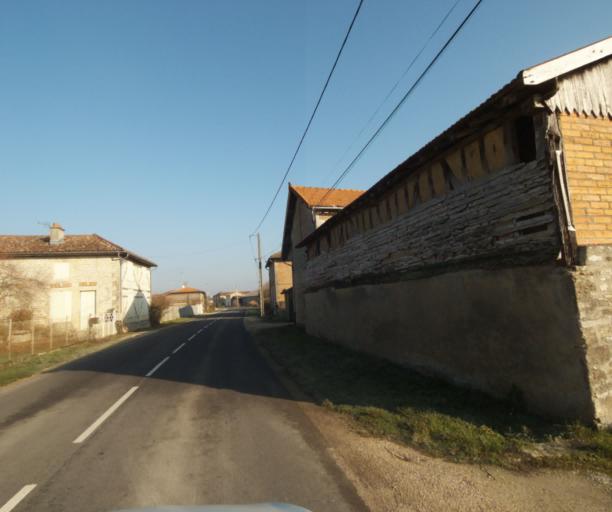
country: FR
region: Champagne-Ardenne
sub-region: Departement de la Haute-Marne
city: Montier-en-Der
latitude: 48.4540
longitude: 4.7681
